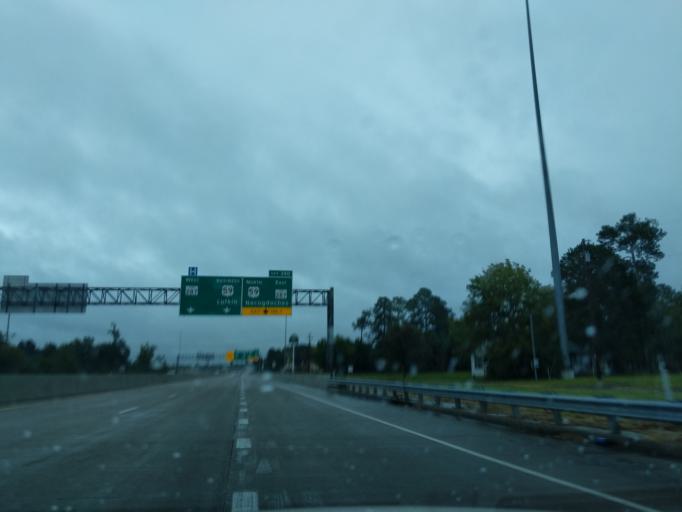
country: US
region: Texas
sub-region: Angelina County
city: Lufkin
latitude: 31.3024
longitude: -94.7268
